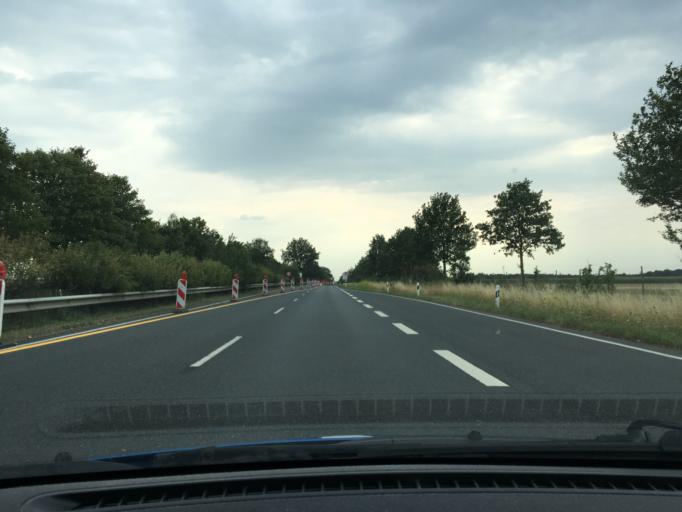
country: DE
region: Lower Saxony
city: Burgdorf
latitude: 52.4952
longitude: 10.0004
